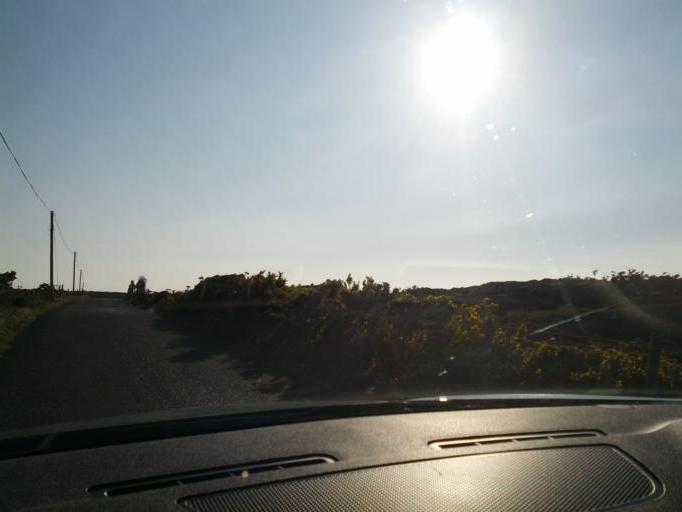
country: IE
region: Connaught
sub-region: County Galway
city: Clifden
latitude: 53.3704
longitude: -9.8554
